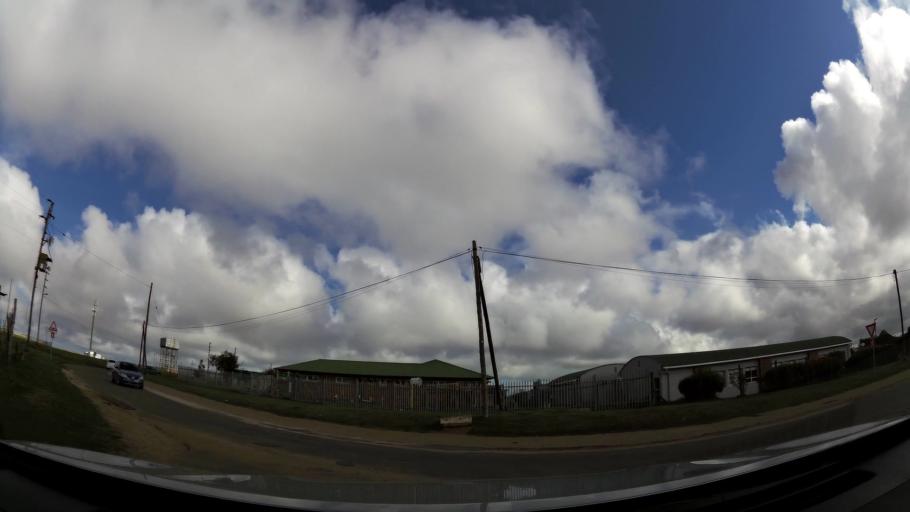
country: ZA
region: Western Cape
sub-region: Eden District Municipality
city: Plettenberg Bay
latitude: -34.0523
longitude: 23.3222
